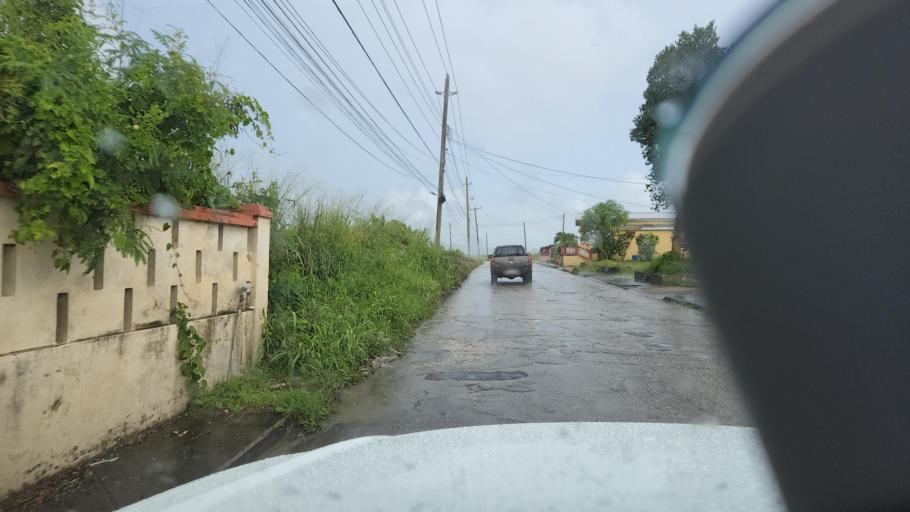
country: BB
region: Saint Michael
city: Bridgetown
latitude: 13.1179
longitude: -59.5729
